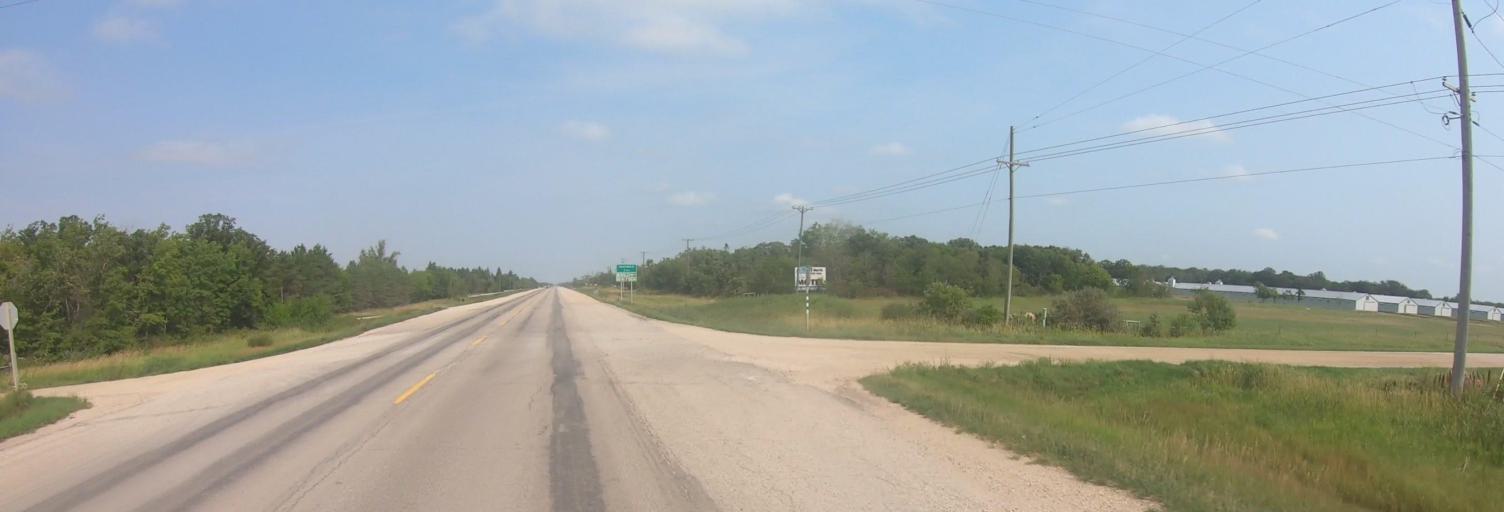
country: CA
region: Manitoba
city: Steinbach
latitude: 49.4877
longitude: -96.6912
